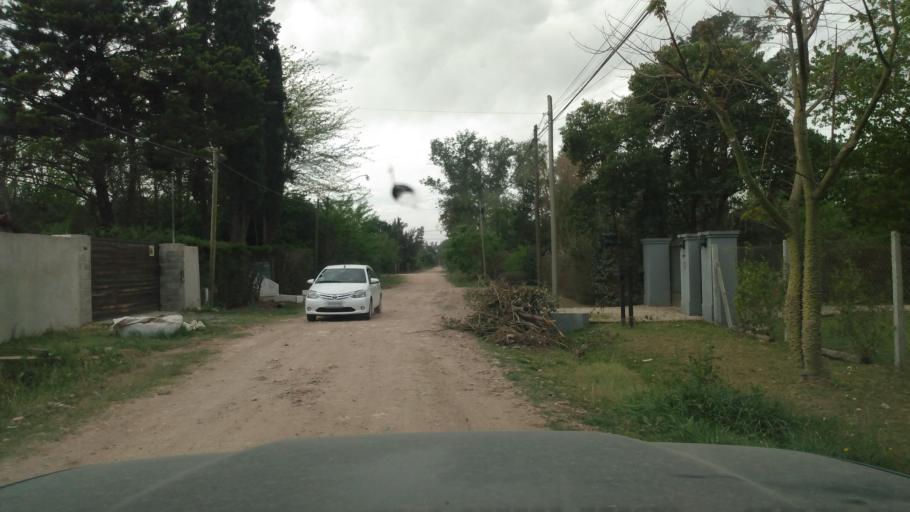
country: AR
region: Buenos Aires
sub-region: Partido de Lujan
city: Lujan
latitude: -34.5918
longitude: -59.1373
